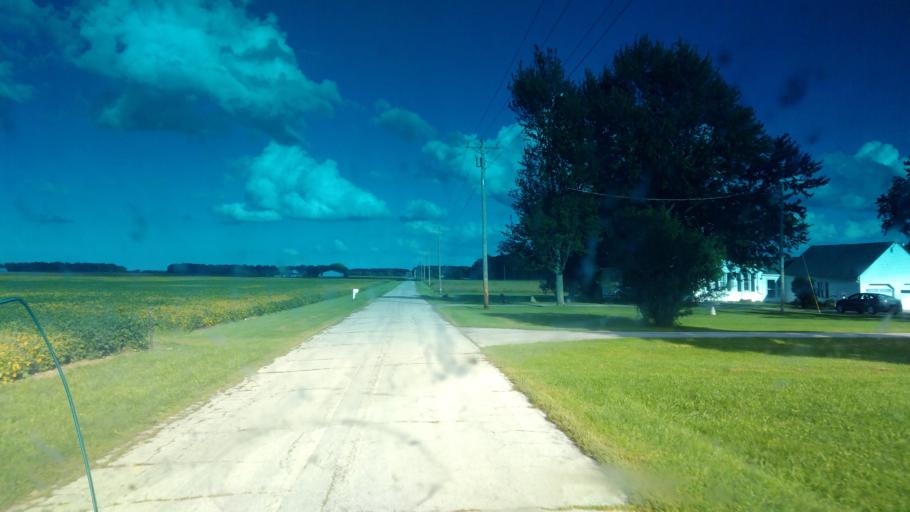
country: US
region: Ohio
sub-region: Hancock County
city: Arlington
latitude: 40.9364
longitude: -83.7588
